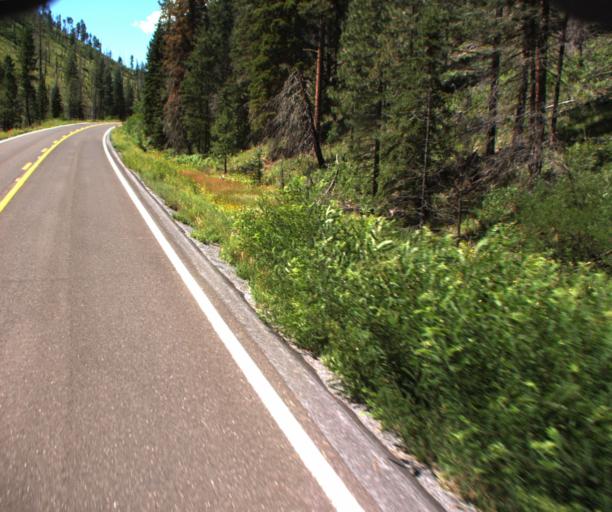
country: US
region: Arizona
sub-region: Apache County
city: Eagar
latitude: 33.6622
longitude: -109.2624
